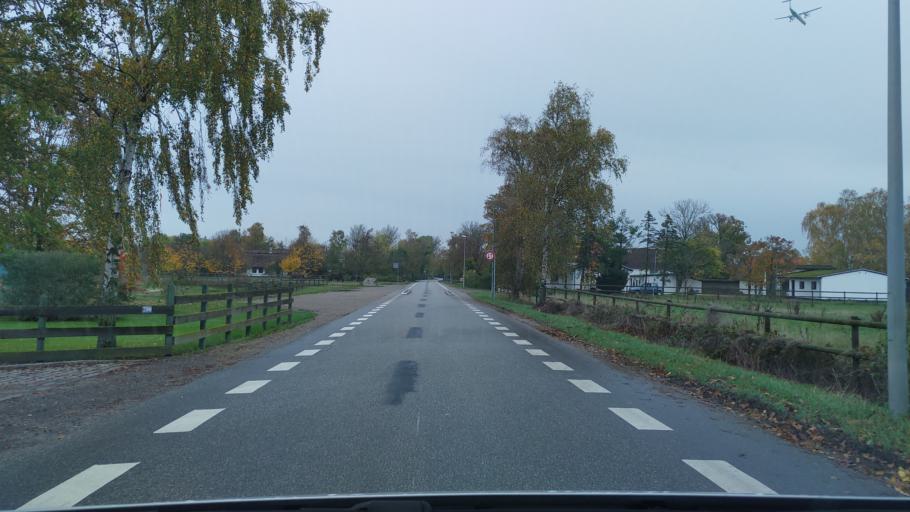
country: DK
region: Capital Region
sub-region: Tarnby Kommune
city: Tarnby
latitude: 55.5799
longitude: 12.6007
